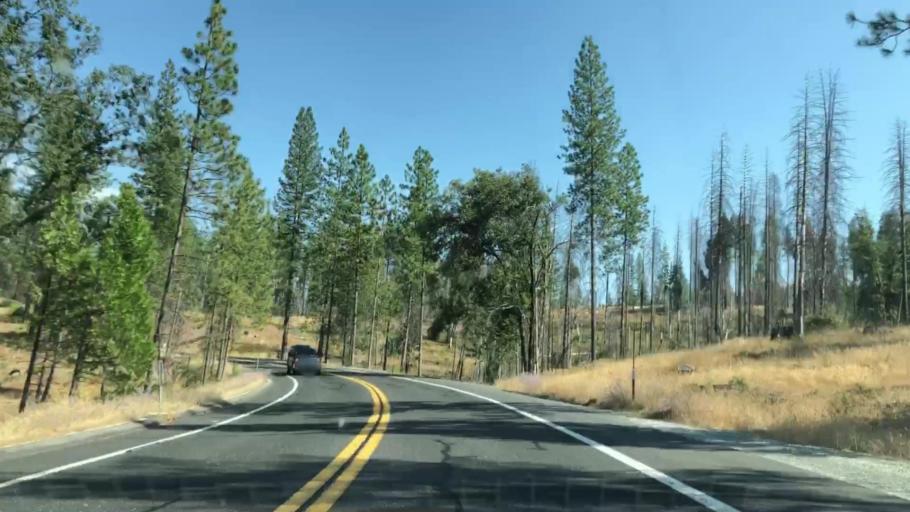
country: US
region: California
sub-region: Mariposa County
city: Midpines
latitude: 37.8151
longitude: -119.9096
